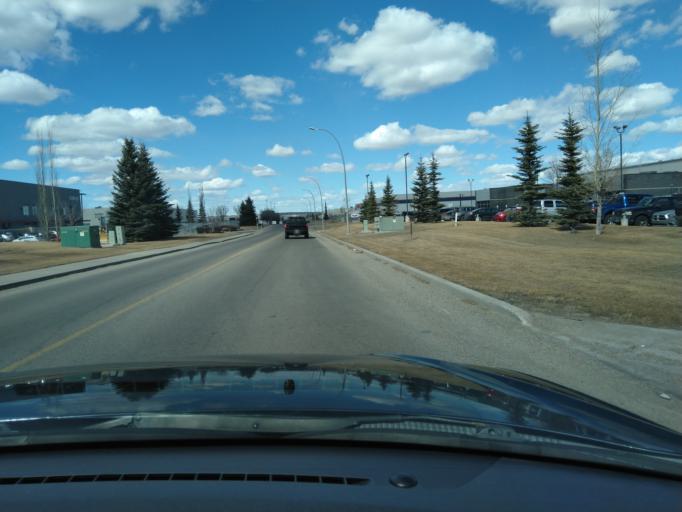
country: CA
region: Alberta
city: Calgary
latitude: 51.1186
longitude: -114.0320
